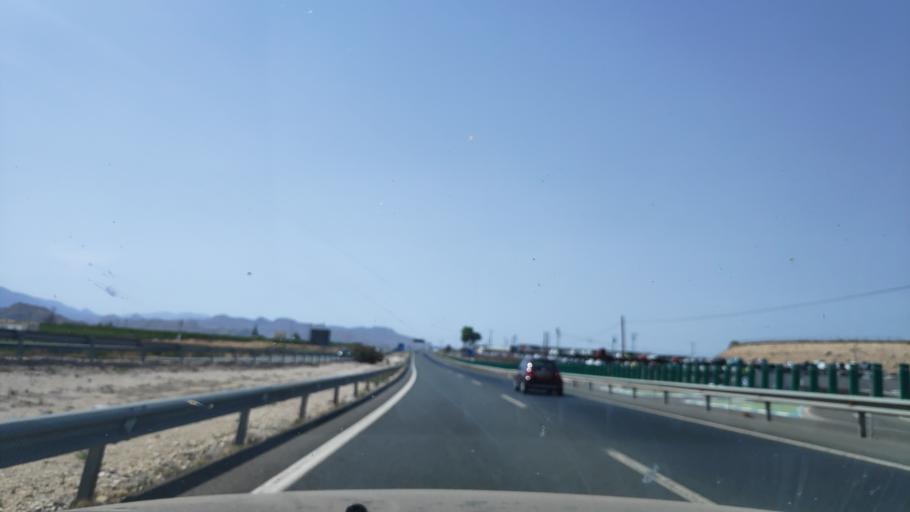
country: ES
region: Murcia
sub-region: Murcia
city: Lorqui
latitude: 38.1164
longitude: -1.2423
